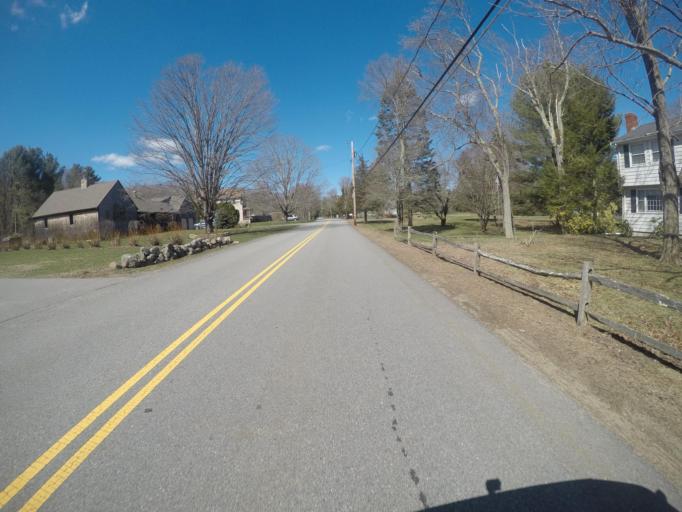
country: US
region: Massachusetts
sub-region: Bristol County
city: Easton
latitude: 42.0071
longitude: -71.0970
